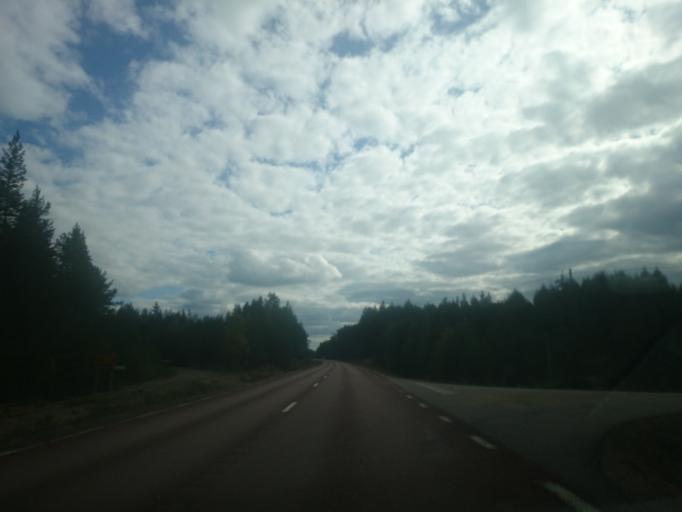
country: SE
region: Gaevleborg
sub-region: Ljusdals Kommun
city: Farila
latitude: 61.8325
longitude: 15.7510
